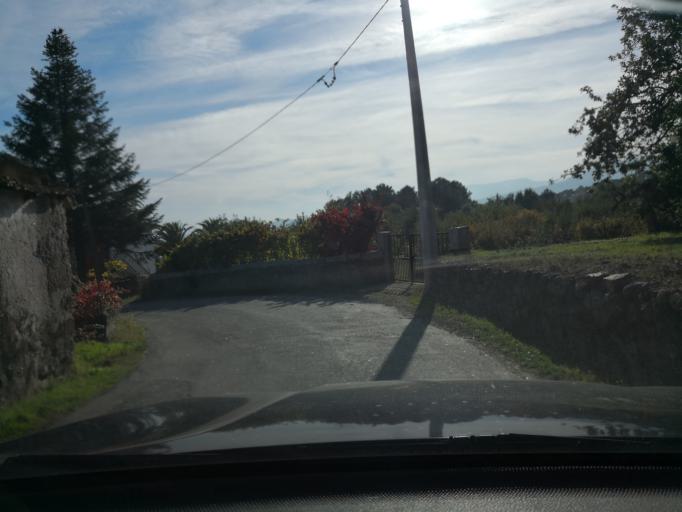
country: PT
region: Vila Real
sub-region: Vila Real
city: Vila Real
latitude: 41.3325
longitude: -7.7428
